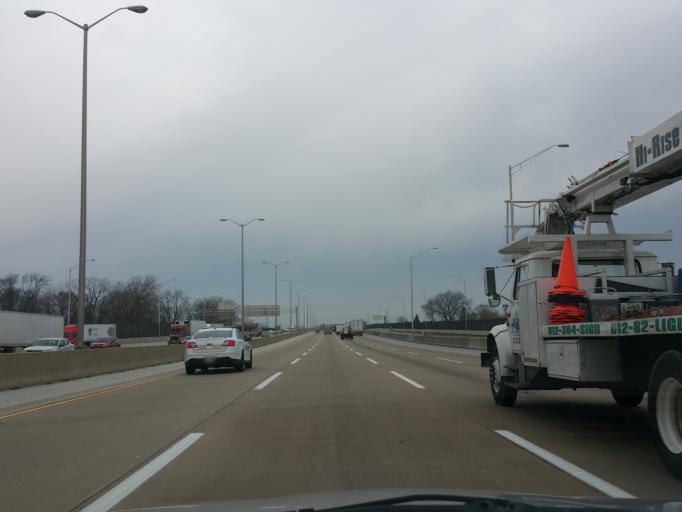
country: US
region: Illinois
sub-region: Cook County
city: Posen
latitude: 41.6220
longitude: -87.6889
